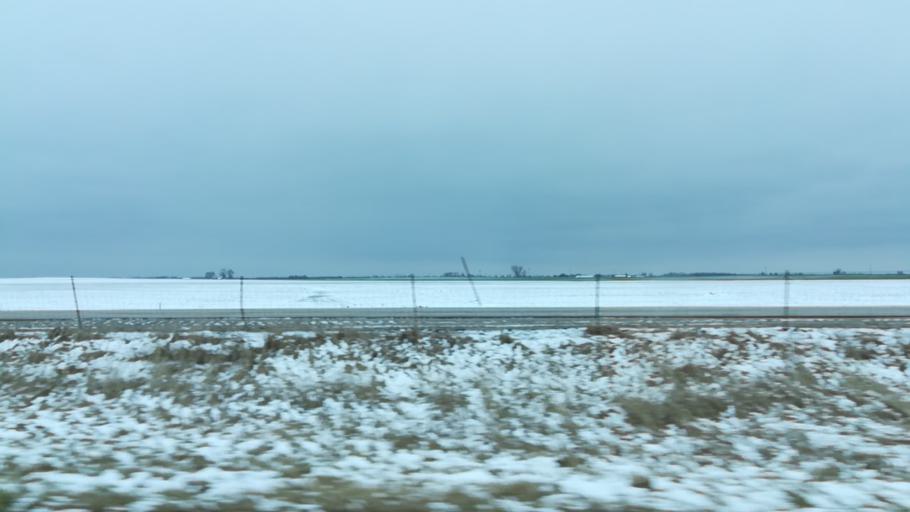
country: US
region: Illinois
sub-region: Madison County
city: Highland
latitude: 38.8142
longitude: -89.5694
